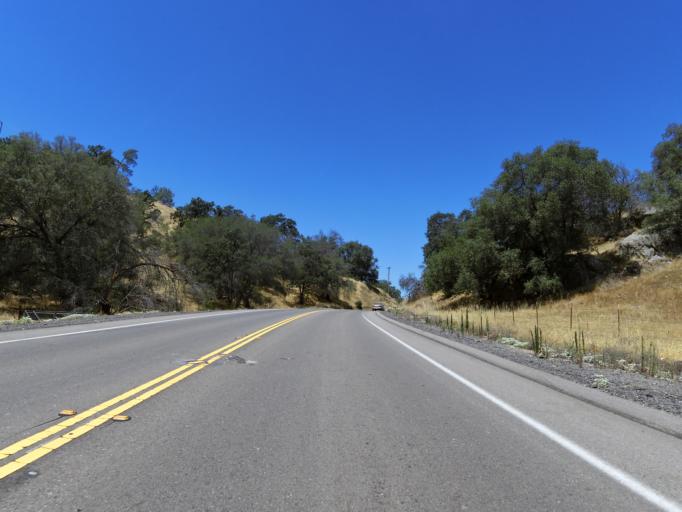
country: US
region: California
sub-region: Fresno County
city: Clovis
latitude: 36.9795
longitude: -119.6318
